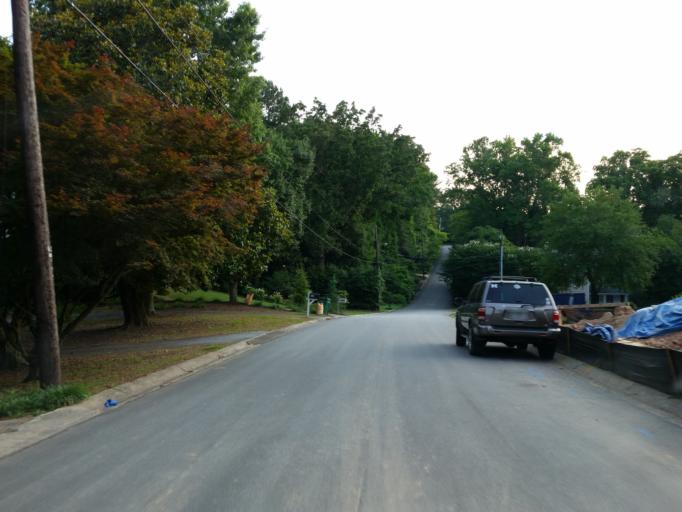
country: US
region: Georgia
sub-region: Cobb County
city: Vinings
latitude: 33.8655
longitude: -84.4624
